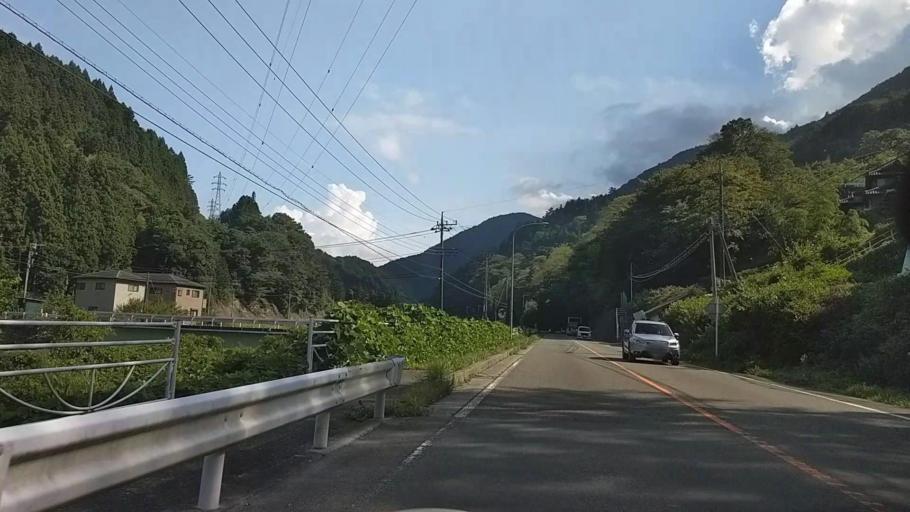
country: JP
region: Shizuoka
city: Fujinomiya
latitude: 35.3395
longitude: 138.4244
